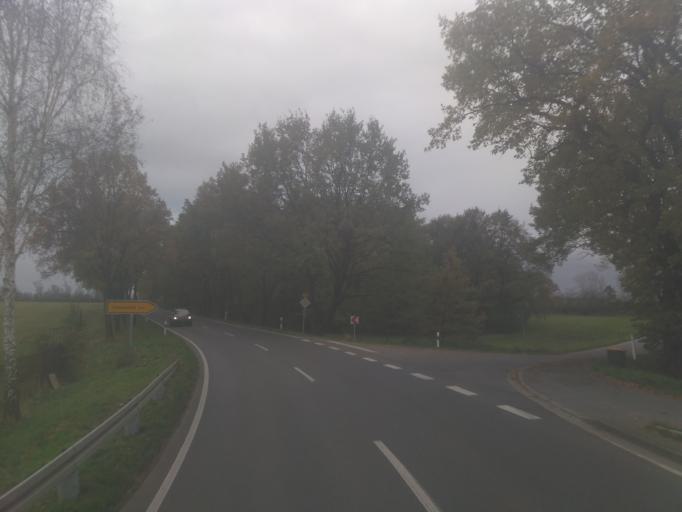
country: DE
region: Saxony
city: Zabeltitz
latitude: 51.3415
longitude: 13.5370
